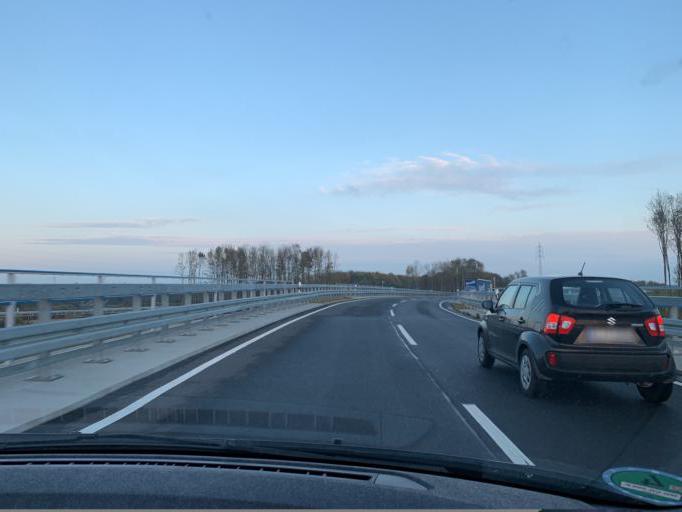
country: DE
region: North Rhine-Westphalia
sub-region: Regierungsbezirk Dusseldorf
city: Juchen
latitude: 51.0917
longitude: 6.4789
